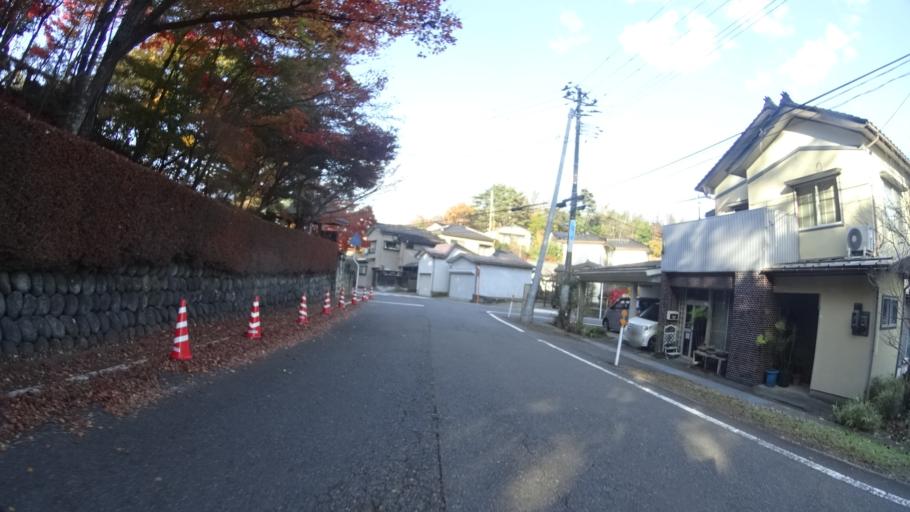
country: JP
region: Niigata
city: Kashiwazaki
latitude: 37.3596
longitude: 138.5456
